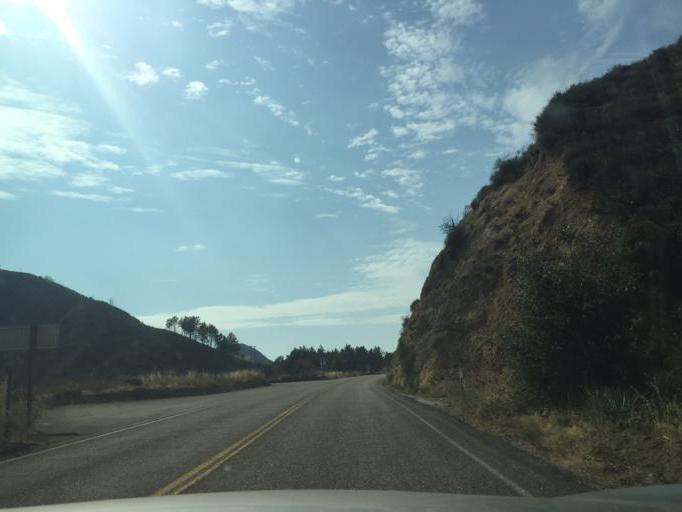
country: US
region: California
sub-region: Los Angeles County
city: La Canada Flintridge
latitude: 34.2697
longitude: -118.1492
